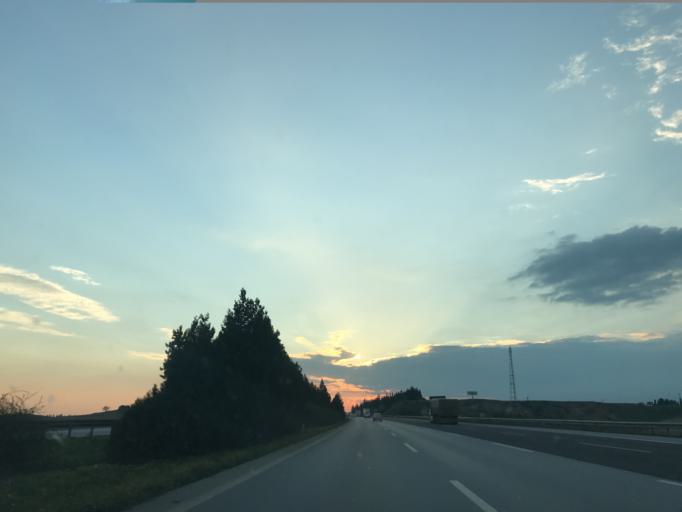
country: TR
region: Mersin
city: Yenice
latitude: 37.0188
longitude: 35.0102
